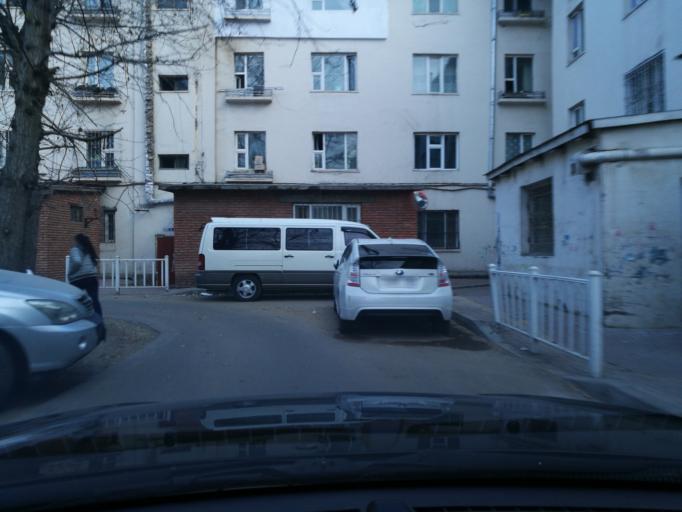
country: MN
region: Ulaanbaatar
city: Ulaanbaatar
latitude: 47.9267
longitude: 106.9200
